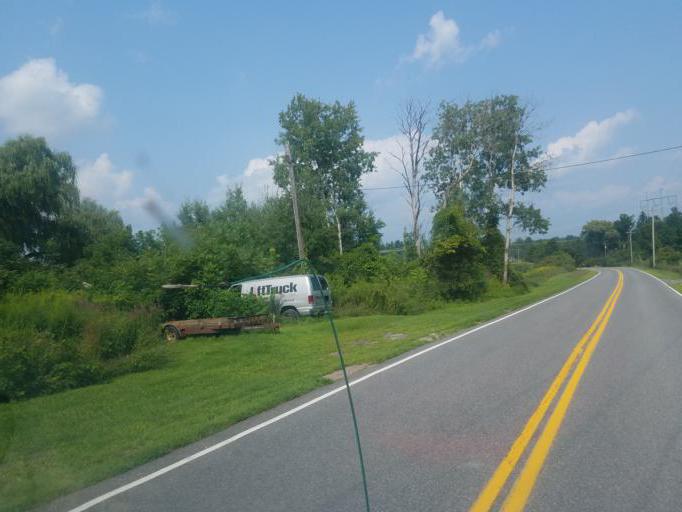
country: US
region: New York
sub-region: Montgomery County
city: Fonda
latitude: 42.9114
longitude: -74.3305
